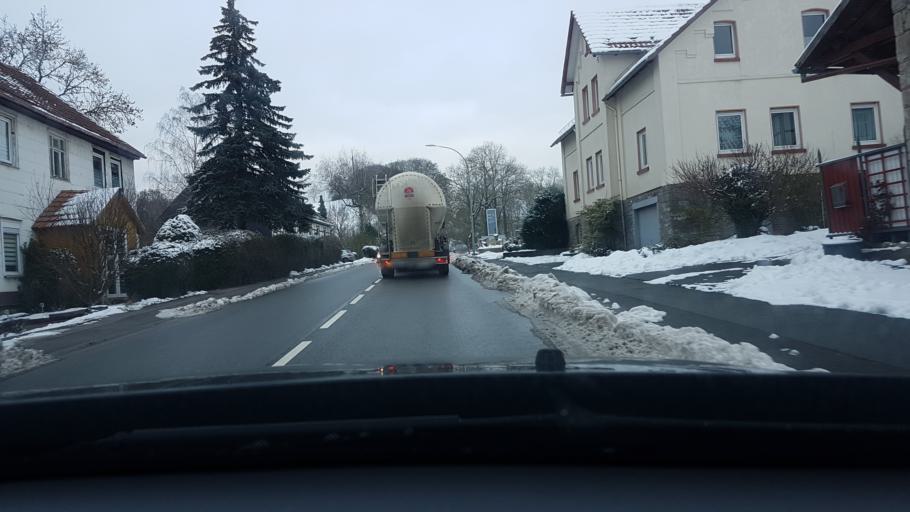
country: DE
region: Hesse
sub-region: Regierungsbezirk Kassel
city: Korbach
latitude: 51.2890
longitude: 8.7990
